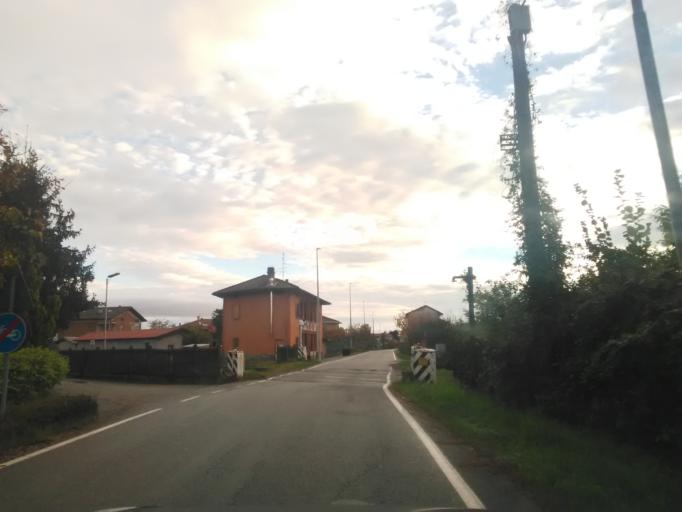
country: IT
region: Piedmont
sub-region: Provincia di Vercelli
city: Rovasenda
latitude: 45.5390
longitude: 8.3179
